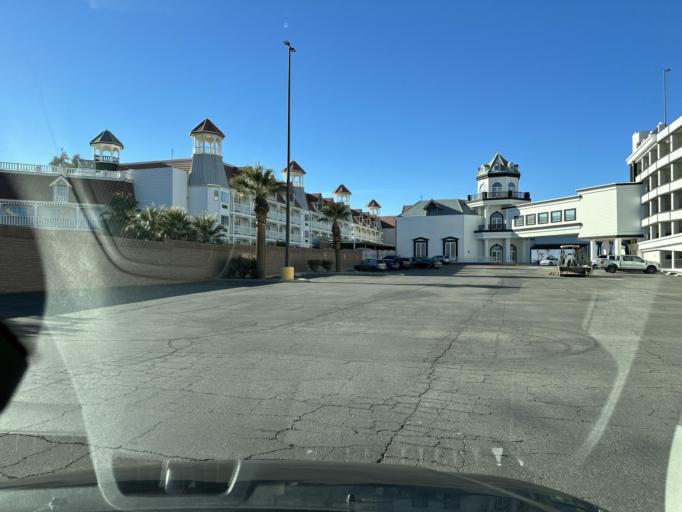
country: US
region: Nevada
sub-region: Clark County
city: Sandy Valley
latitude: 35.6113
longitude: -115.3849
